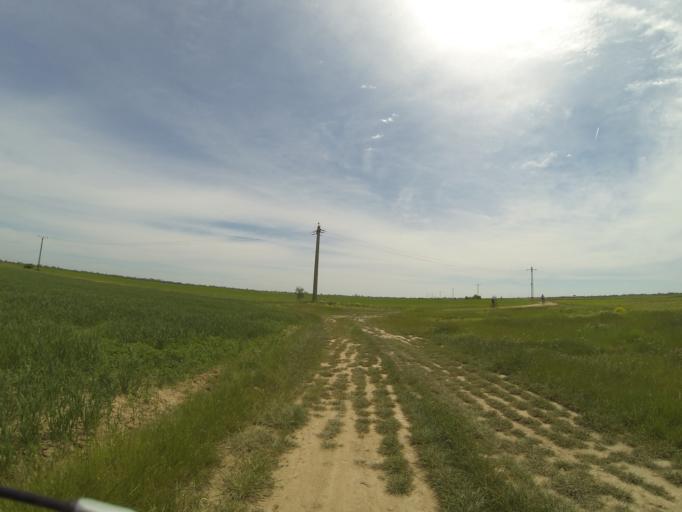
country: RO
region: Dolj
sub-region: Comuna Ghindeni
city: Ghindeni
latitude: 44.2062
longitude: 23.9577
